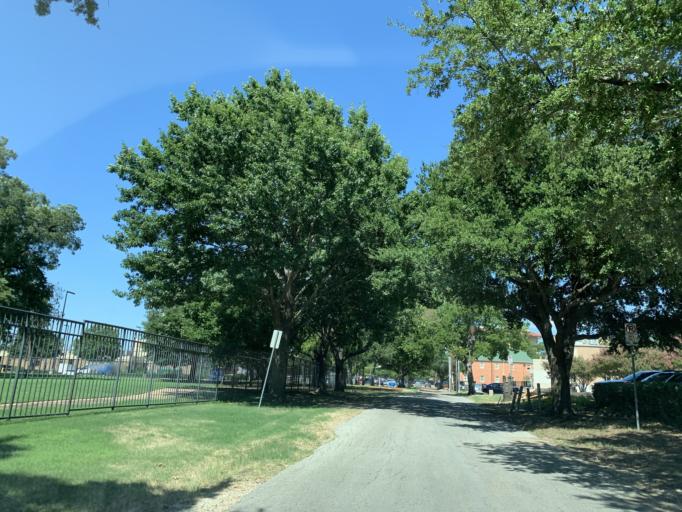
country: US
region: Texas
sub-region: Dallas County
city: Dallas
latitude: 32.7920
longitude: -96.7830
